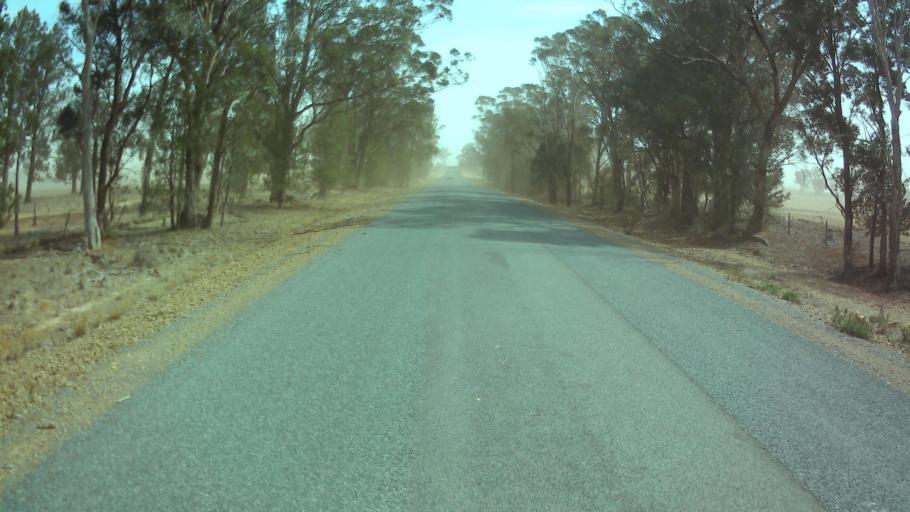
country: AU
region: New South Wales
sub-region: Weddin
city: Grenfell
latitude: -33.7531
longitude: 147.9903
